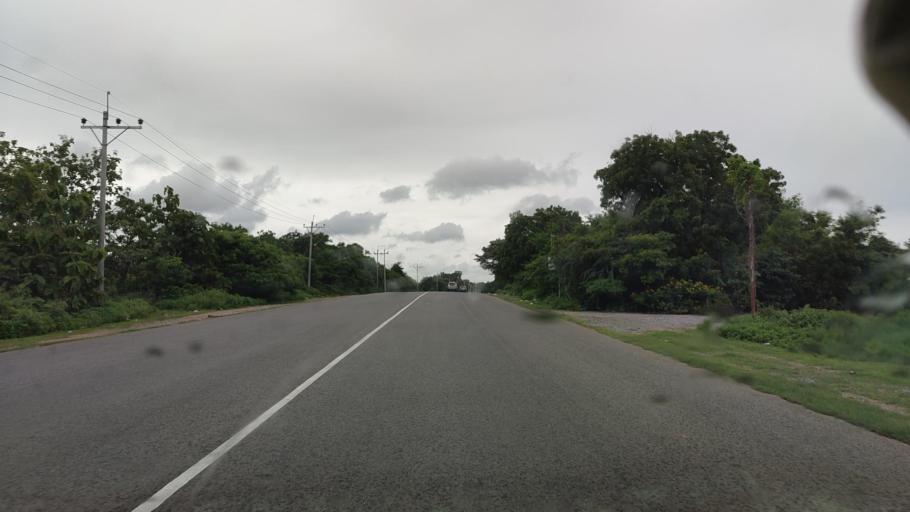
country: MM
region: Mandalay
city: Meiktila
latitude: 20.8196
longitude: 95.9046
